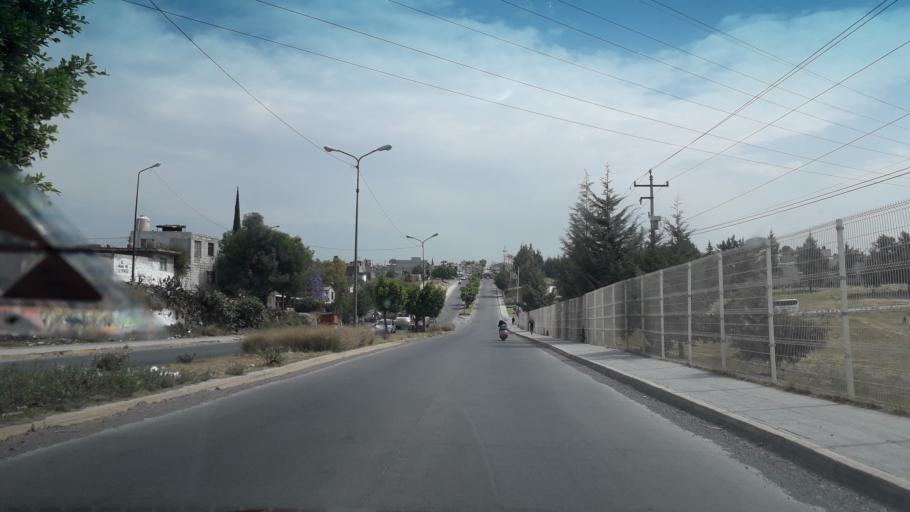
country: MX
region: Puebla
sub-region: Puebla
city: El Capulo (La Quebradora)
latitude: 18.9572
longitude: -98.2690
